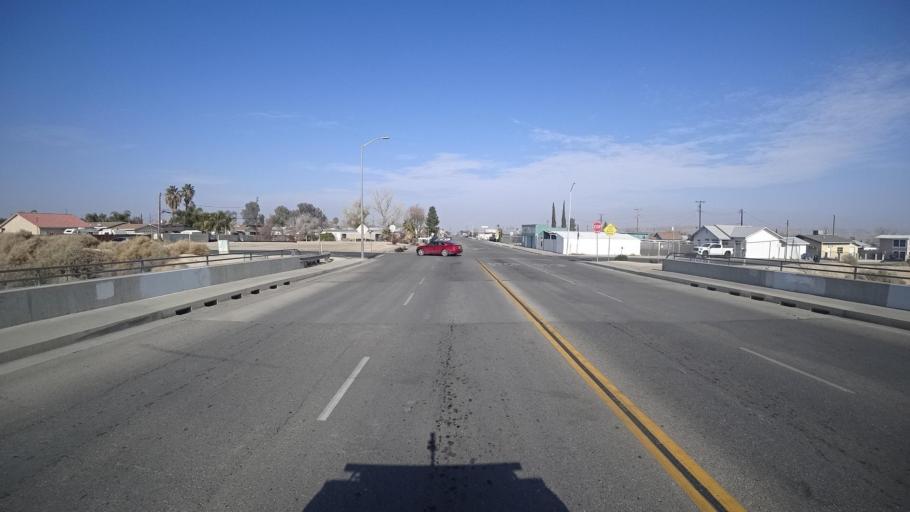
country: US
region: California
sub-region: Kern County
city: Ford City
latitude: 35.1511
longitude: -119.4563
